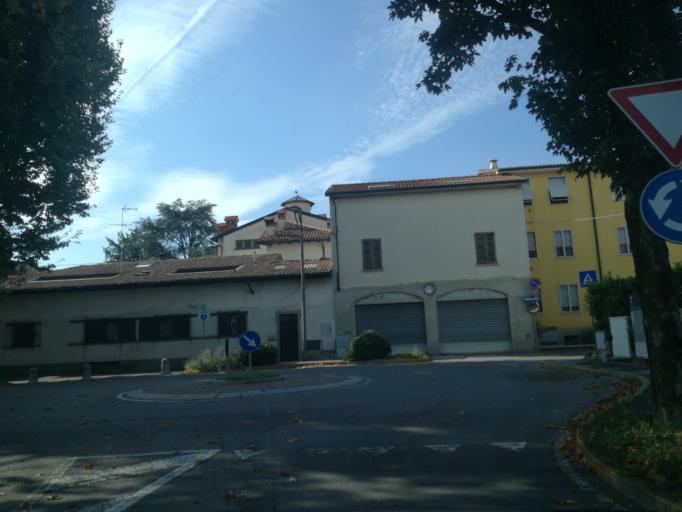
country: IT
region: Lombardy
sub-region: Provincia di Monza e Brianza
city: Velasca
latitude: 45.6347
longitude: 9.3513
